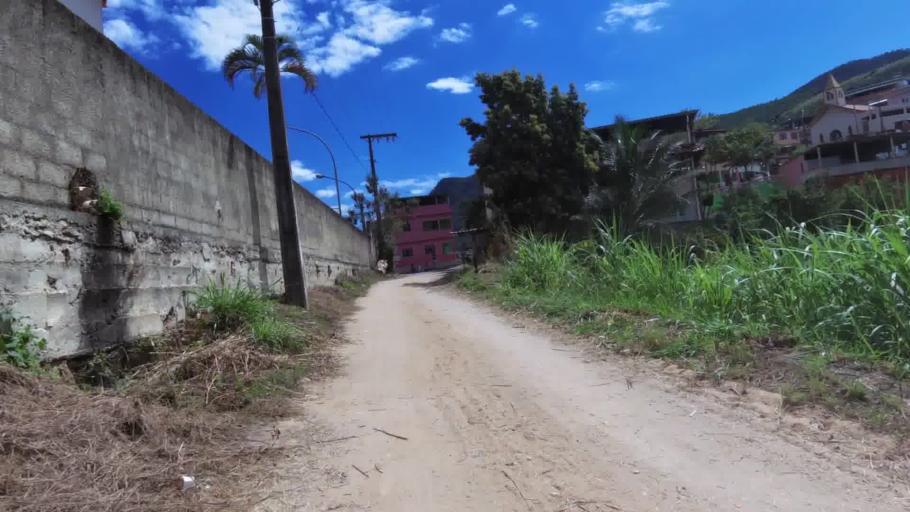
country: BR
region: Espirito Santo
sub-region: Rio Novo Do Sul
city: Rio Novo do Sul
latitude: -20.8680
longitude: -40.9425
